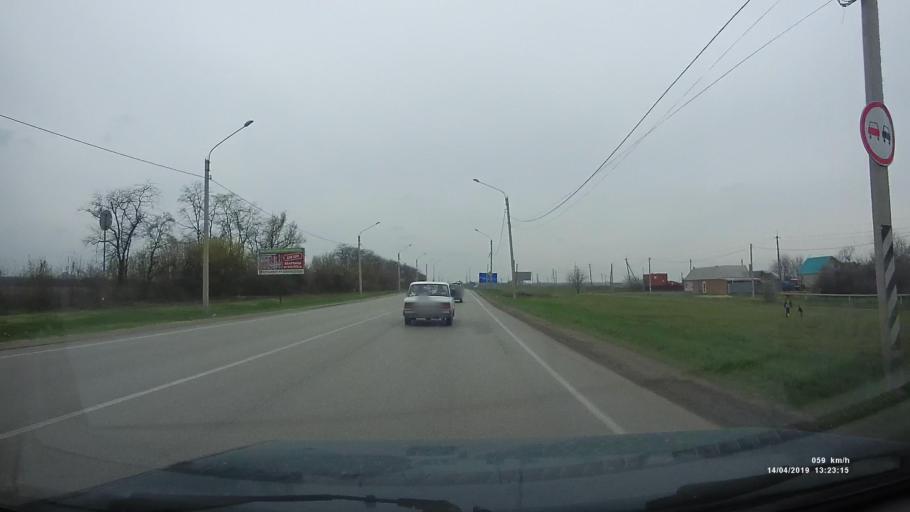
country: RU
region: Rostov
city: Kuleshovka
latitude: 47.0834
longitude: 39.5031
